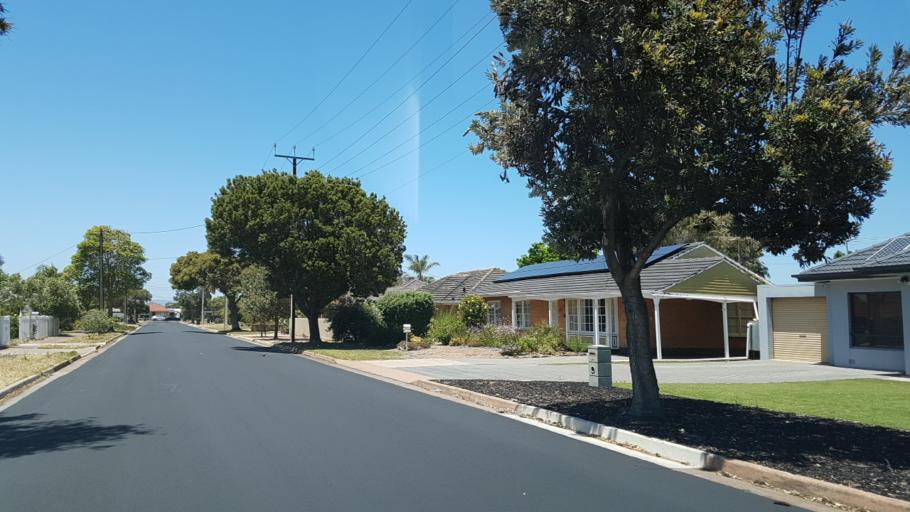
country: AU
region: South Australia
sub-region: Charles Sturt
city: West Lakes Shore
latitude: -34.8552
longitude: 138.4813
